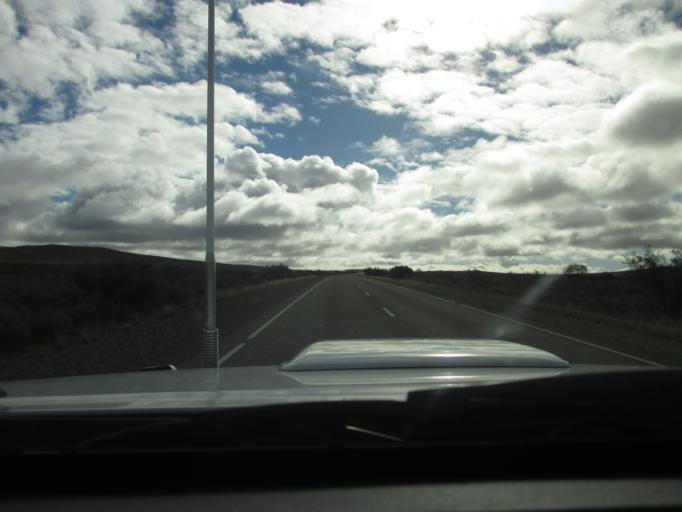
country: AU
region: South Australia
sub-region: Flinders Ranges
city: Quorn
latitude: -32.1964
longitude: 138.5324
